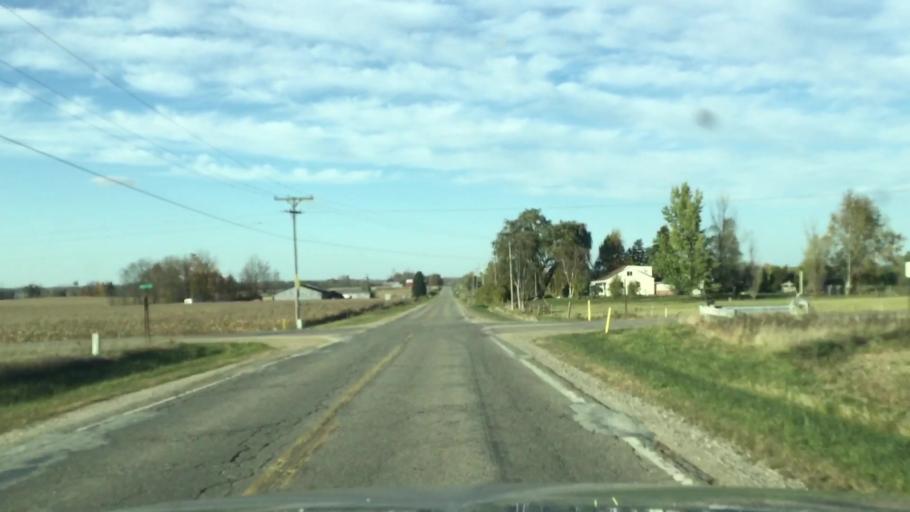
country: US
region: Michigan
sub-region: Lapeer County
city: North Branch
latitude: 43.2668
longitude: -83.1980
